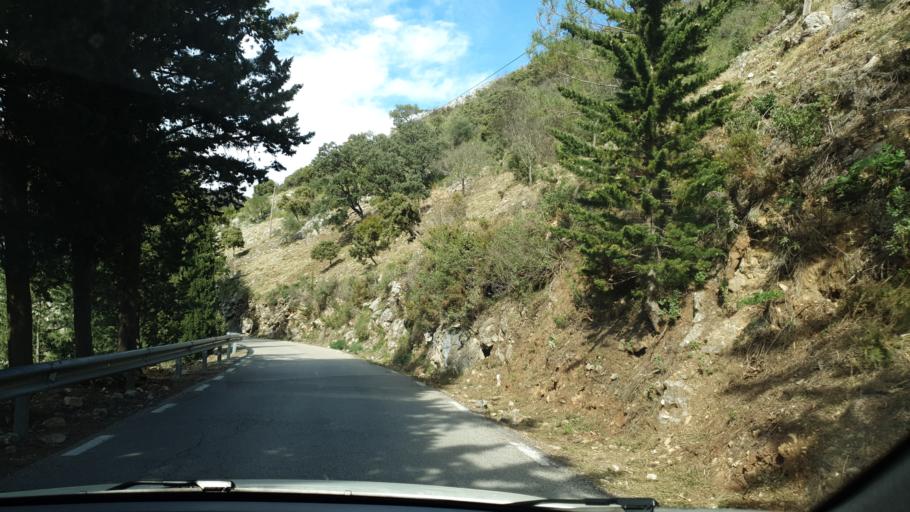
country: ES
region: Andalusia
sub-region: Provincia de Malaga
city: Ojen
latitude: 36.5850
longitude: -4.8817
